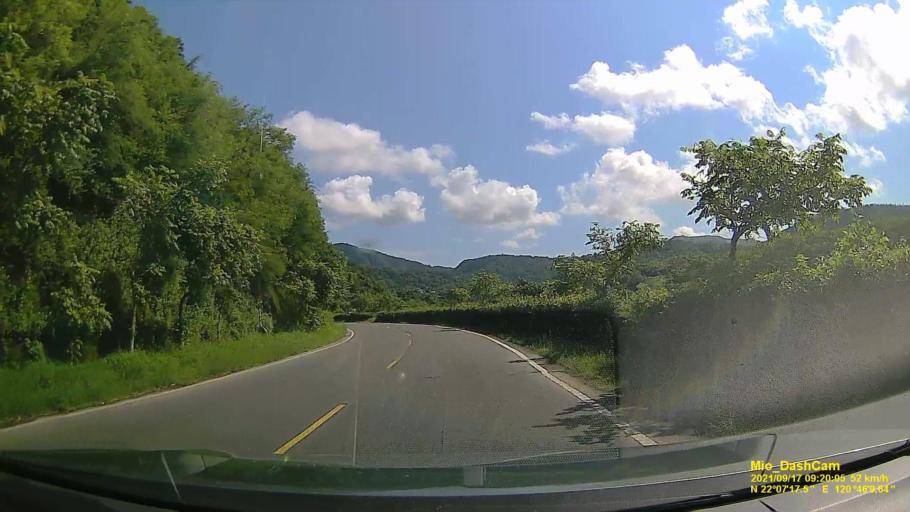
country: TW
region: Taiwan
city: Hengchun
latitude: 22.1216
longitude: 120.7695
